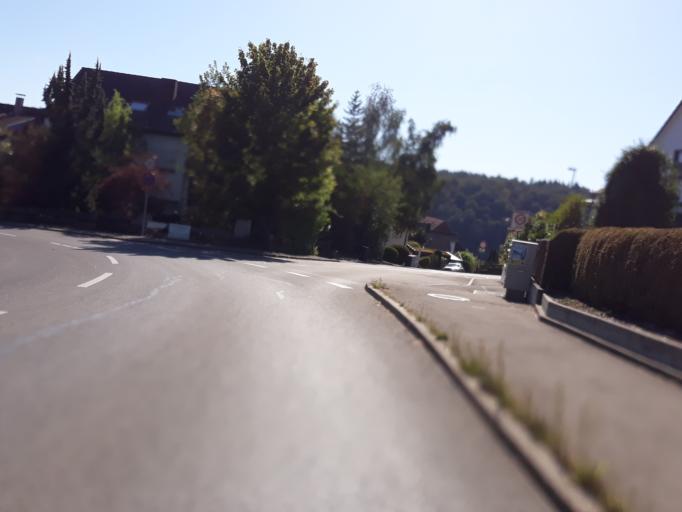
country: DE
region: Baden-Wuerttemberg
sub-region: Regierungsbezirk Stuttgart
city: Aidlingen
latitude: 48.7123
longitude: 8.9159
